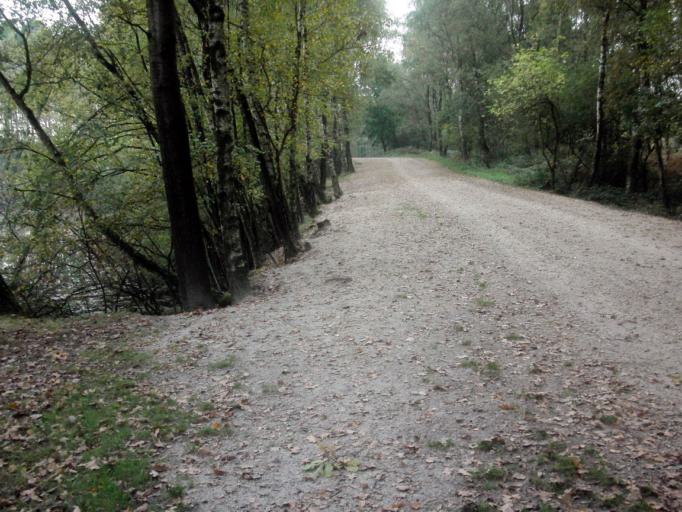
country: DE
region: North Rhine-Westphalia
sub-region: Regierungsbezirk Koln
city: Gangelt
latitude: 50.9524
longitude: 6.0246
